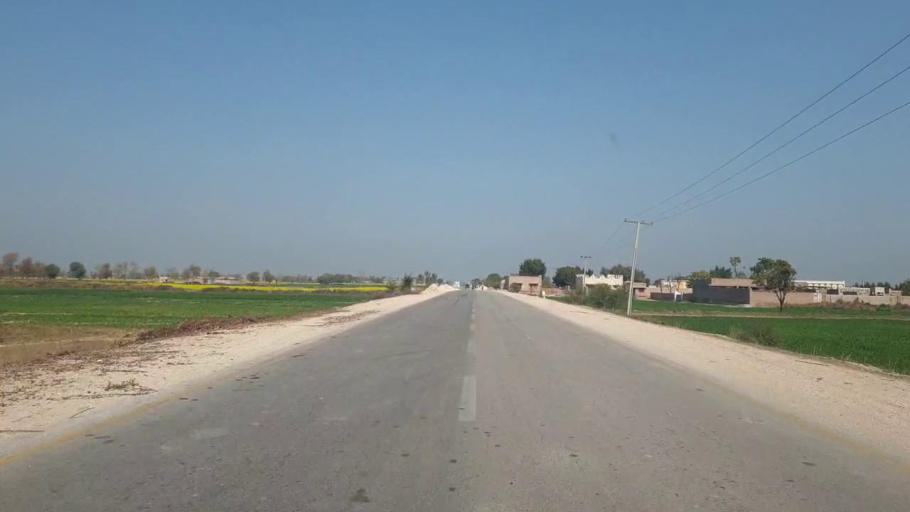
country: PK
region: Sindh
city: Sakrand
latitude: 26.0352
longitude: 68.4009
